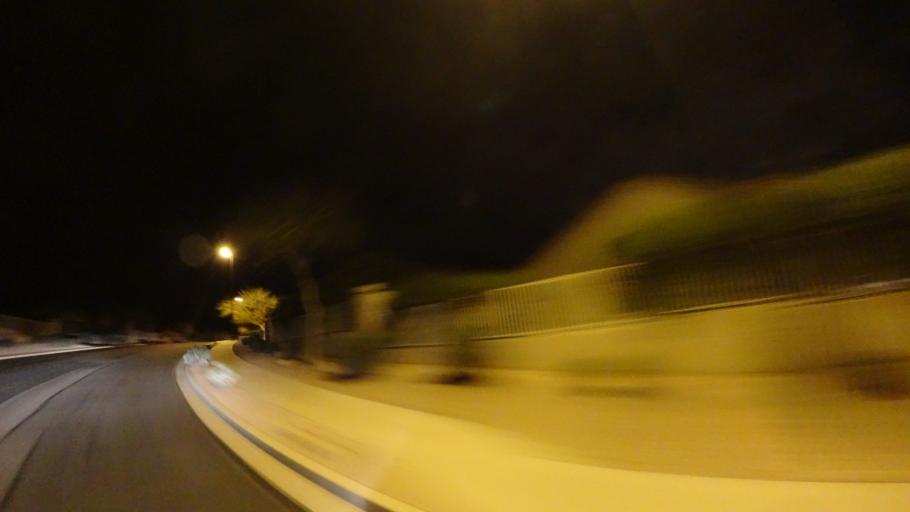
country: US
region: Arizona
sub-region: Maricopa County
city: Fountain Hills
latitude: 33.4939
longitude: -111.6923
